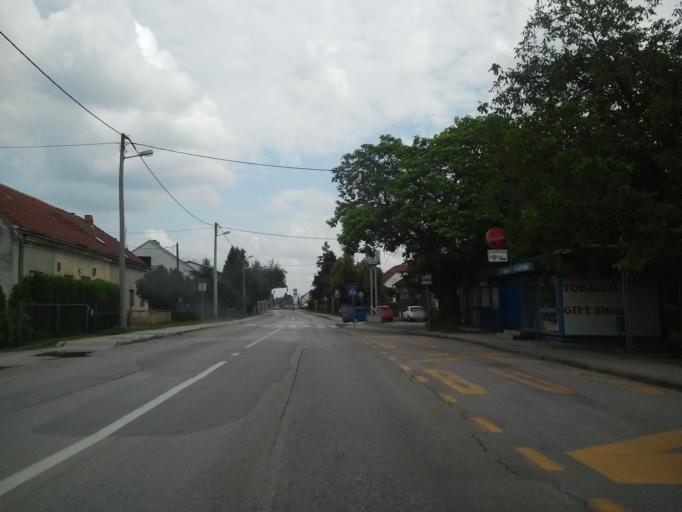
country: HR
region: Grad Zagreb
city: Lucko
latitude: 45.7615
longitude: 15.8818
